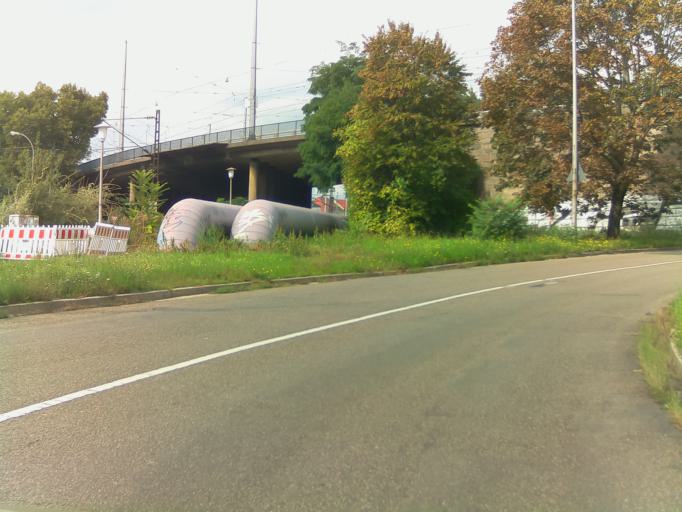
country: DE
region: Rheinland-Pfalz
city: Altrip
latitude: 49.4500
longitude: 8.4994
